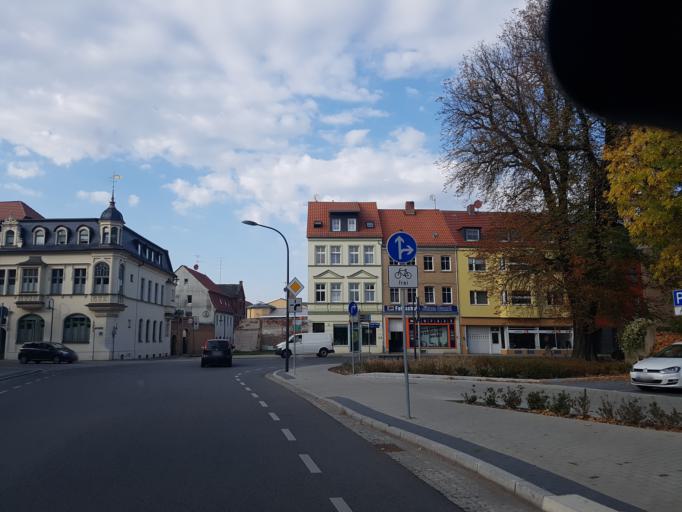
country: DE
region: Brandenburg
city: Finsterwalde
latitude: 51.6300
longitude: 13.7123
